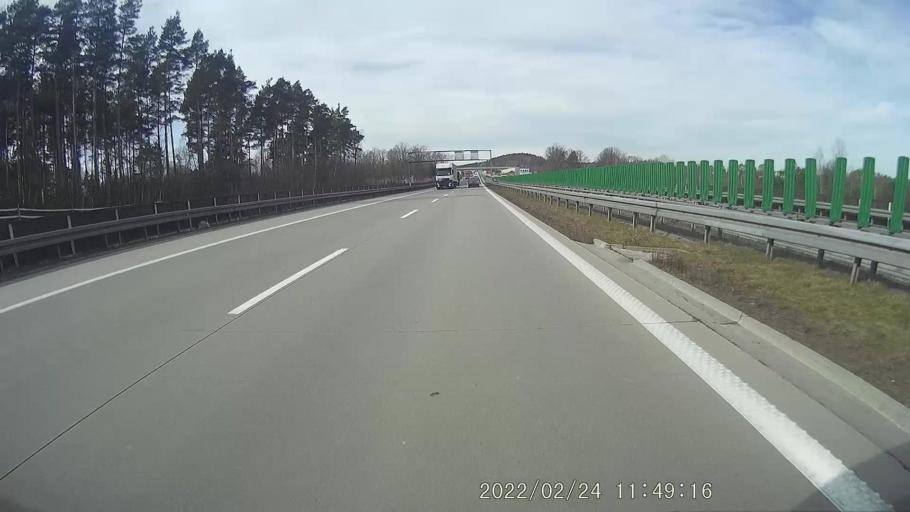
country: PL
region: Lower Silesian Voivodeship
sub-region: Powiat polkowicki
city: Radwanice
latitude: 51.5929
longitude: 15.9588
